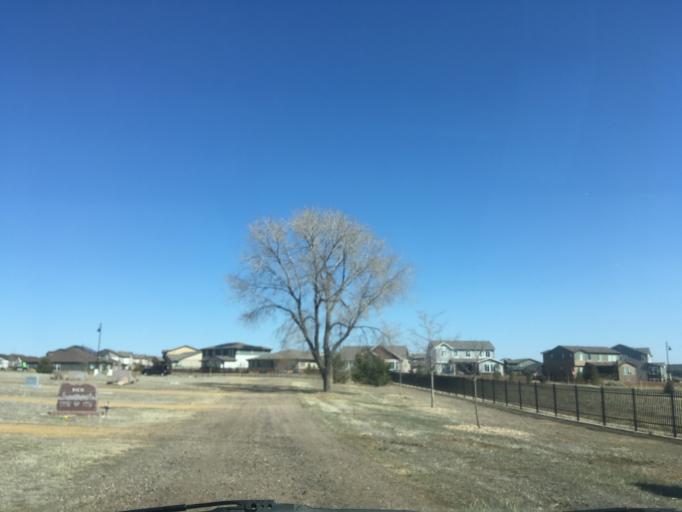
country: US
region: Colorado
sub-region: Boulder County
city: Erie
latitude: 40.0508
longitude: -105.0383
